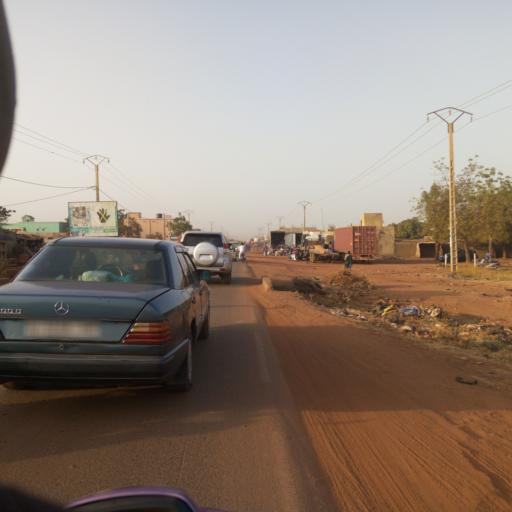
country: ML
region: Bamako
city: Bamako
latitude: 12.6256
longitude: -7.9211
